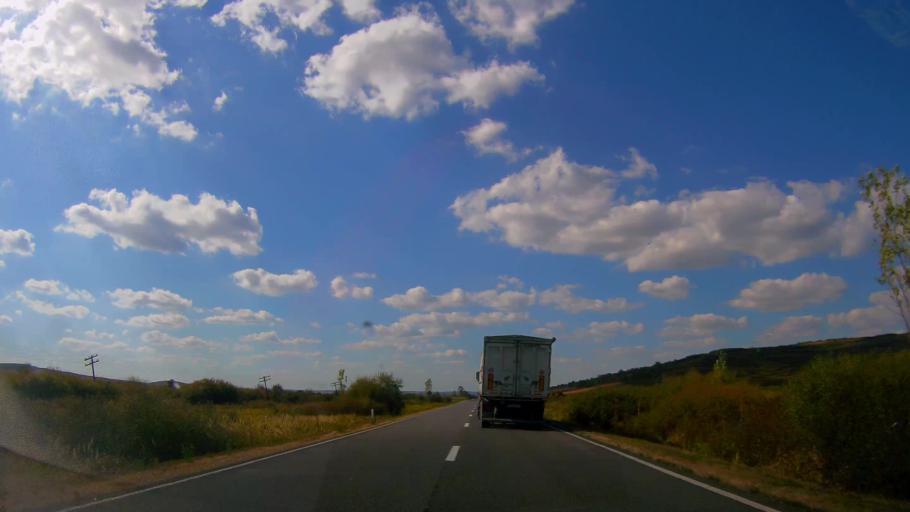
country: RO
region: Salaj
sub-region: Comuna Bocsa
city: Bocsa
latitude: 47.3256
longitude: 22.8770
